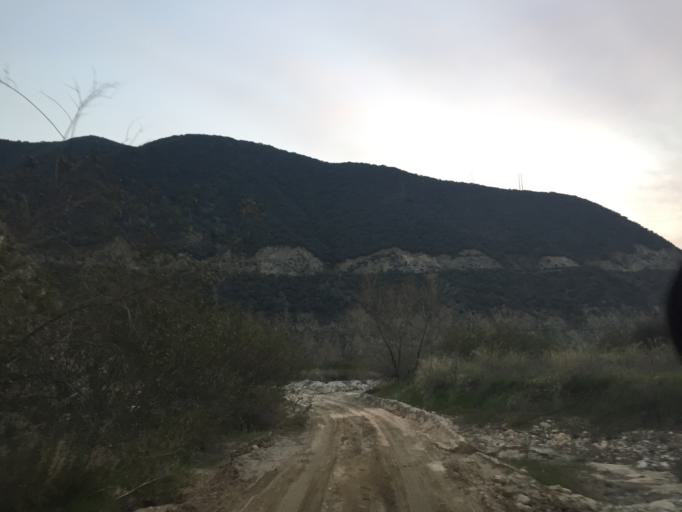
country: US
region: California
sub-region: San Bernardino County
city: Mentone
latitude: 34.1223
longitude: -117.0794
